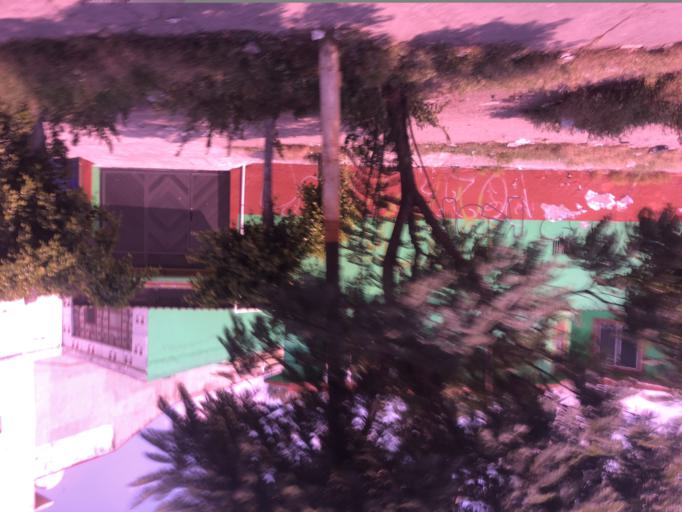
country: MX
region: Mexico
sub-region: Ciudad Nezahualcoyotl
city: Colonia Gustavo Baz Prada
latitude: 19.4535
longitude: -99.0488
